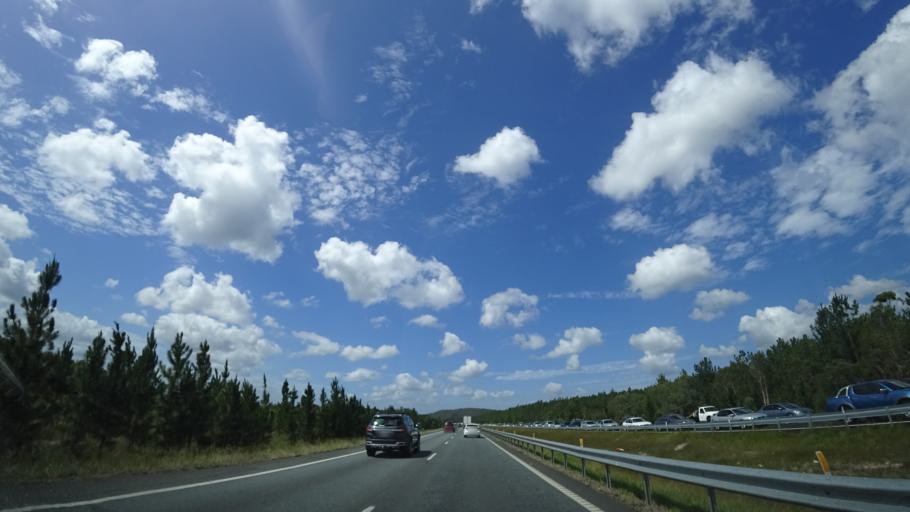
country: AU
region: Queensland
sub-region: Moreton Bay
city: Caboolture
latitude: -26.9540
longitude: 152.9887
